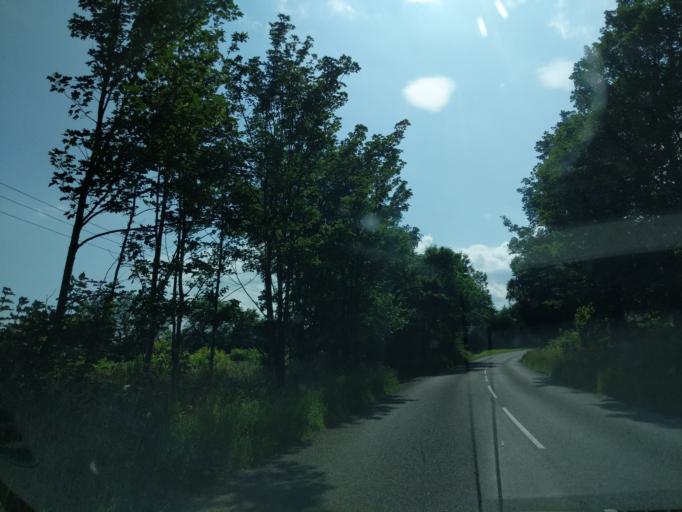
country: GB
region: Scotland
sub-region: Moray
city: Rothes
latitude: 57.5407
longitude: -3.1917
